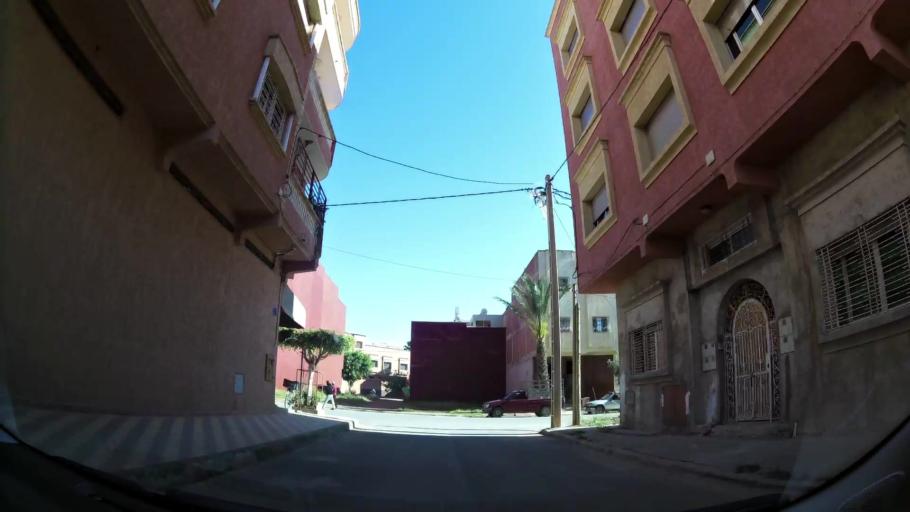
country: MA
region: Oriental
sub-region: Berkane-Taourirt
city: Berkane
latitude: 34.9366
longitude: -2.3364
